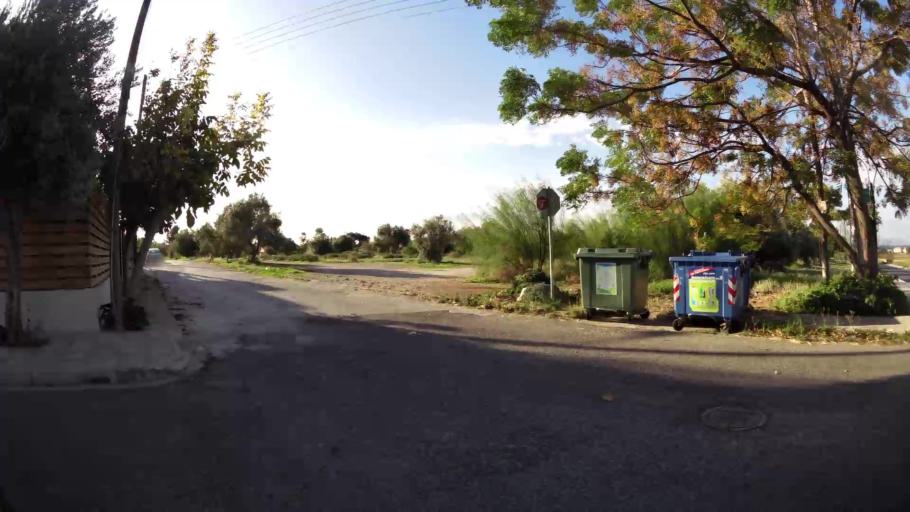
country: GR
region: Attica
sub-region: Nomarchia Athinas
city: Elliniko
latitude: 37.8794
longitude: 23.7456
